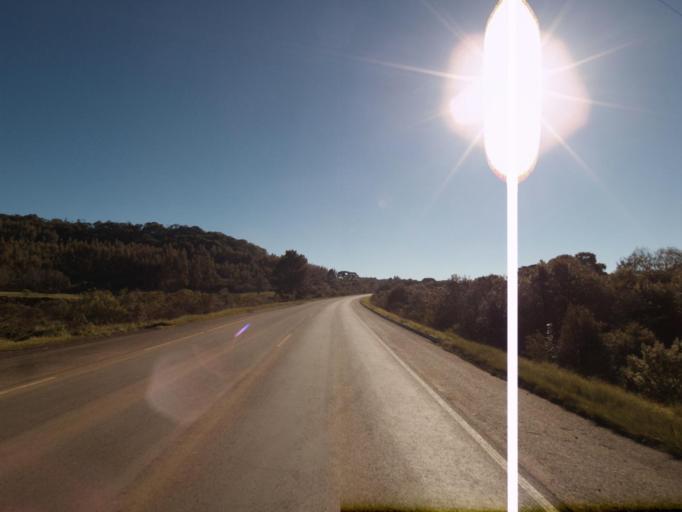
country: BR
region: Santa Catarina
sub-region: Concordia
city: Concordia
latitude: -26.9253
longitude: -51.8105
